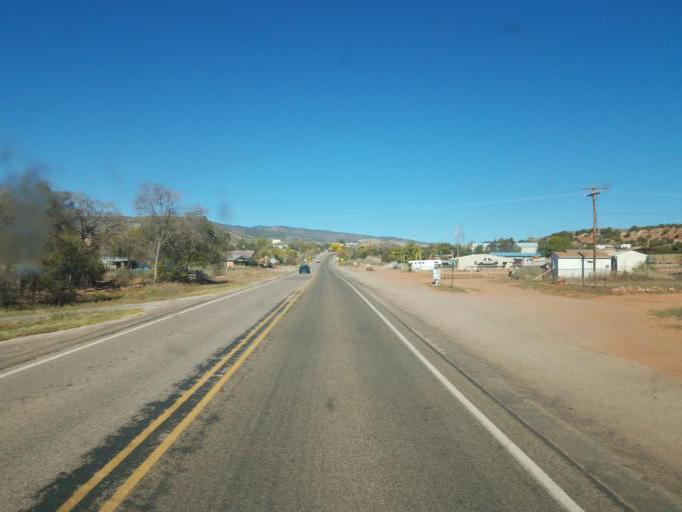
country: US
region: New Mexico
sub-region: Sandoval County
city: Jemez Pueblo
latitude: 35.6527
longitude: -106.7326
